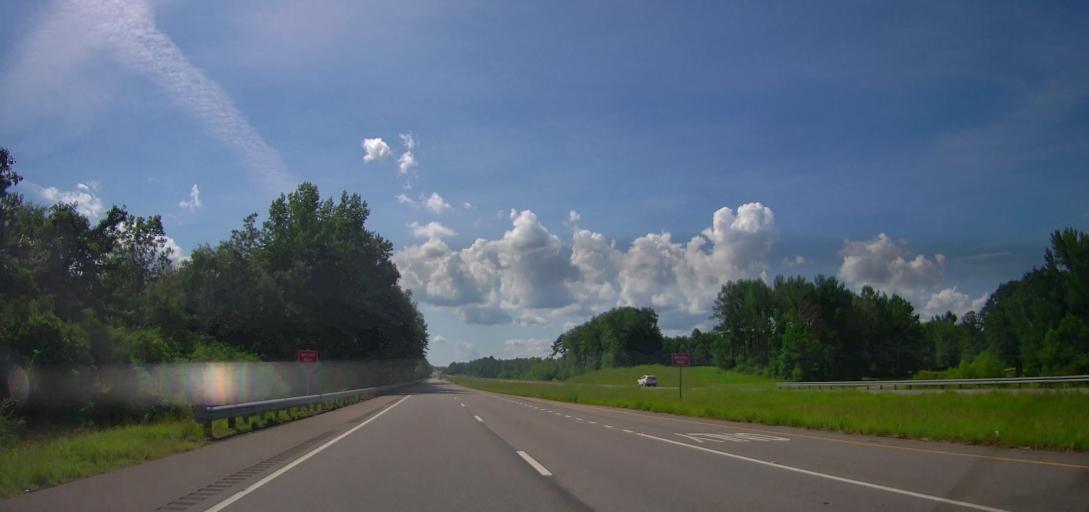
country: US
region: Alabama
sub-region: Pickens County
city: Gordo
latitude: 33.3428
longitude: -87.9436
